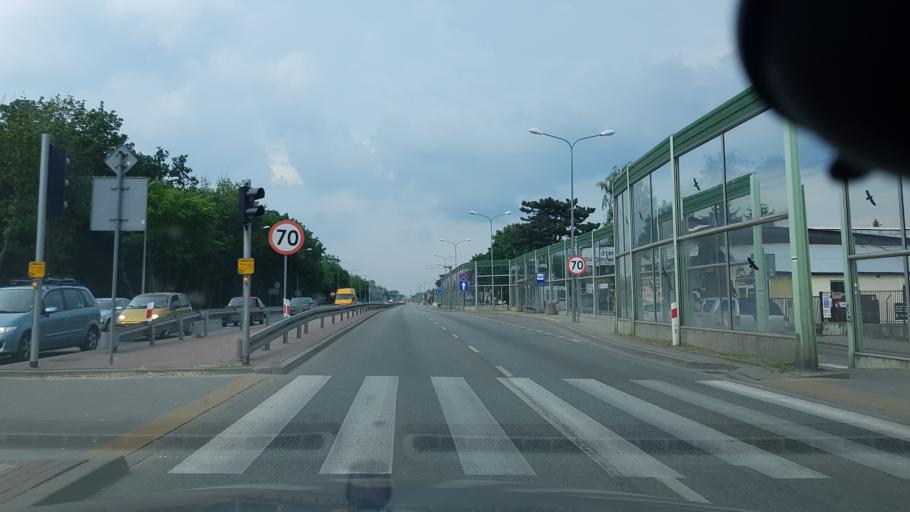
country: PL
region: Masovian Voivodeship
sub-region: Powiat legionowski
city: Legionowo
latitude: 52.3880
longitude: 20.9291
